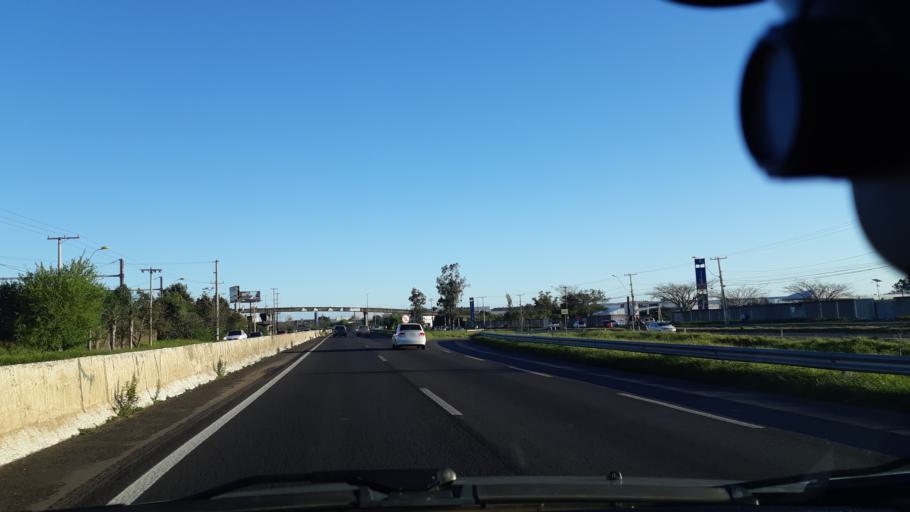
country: BR
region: Rio Grande do Sul
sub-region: Esteio
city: Esteio
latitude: -29.8570
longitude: -51.1805
